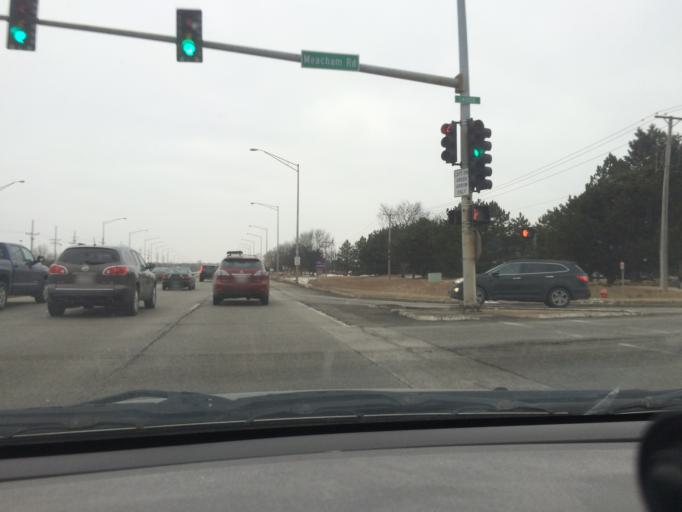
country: US
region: Illinois
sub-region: Cook County
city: Hoffman Estates
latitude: 42.0392
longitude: -88.0453
